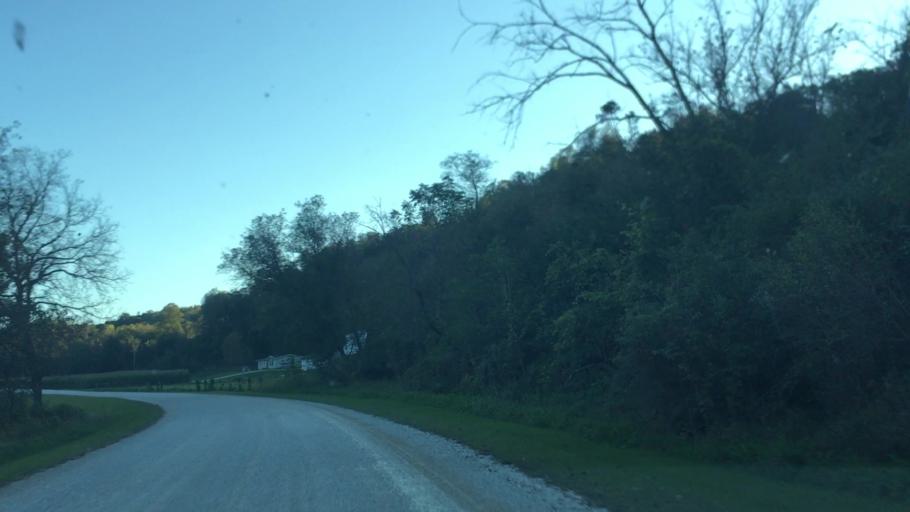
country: US
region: Minnesota
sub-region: Fillmore County
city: Preston
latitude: 43.7603
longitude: -92.0298
